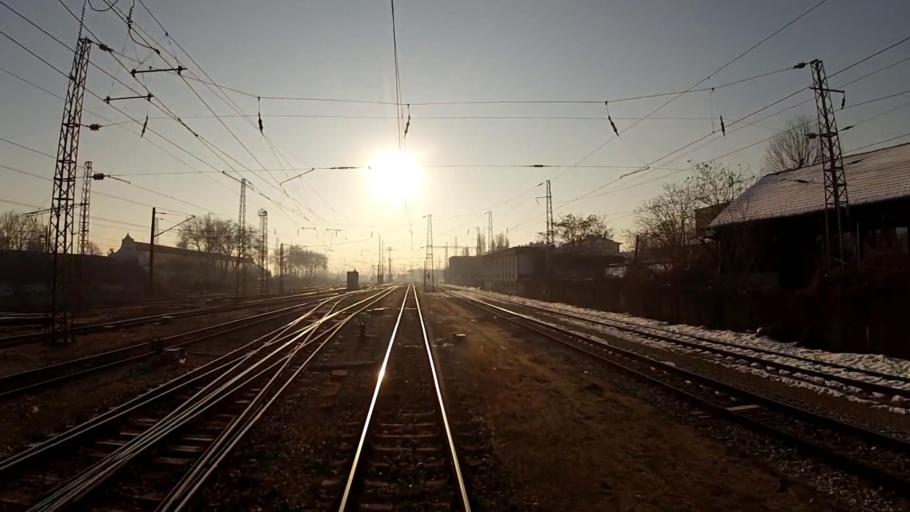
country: BG
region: Sofia-Capital
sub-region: Stolichna Obshtina
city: Sofia
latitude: 42.7231
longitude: 23.2945
